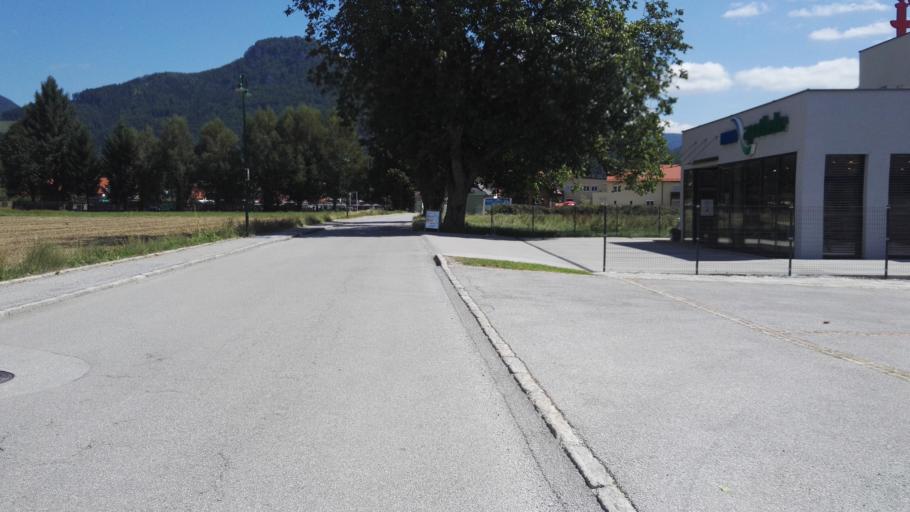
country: AT
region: Styria
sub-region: Politischer Bezirk Graz-Umgebung
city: Frohnleiten
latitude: 47.2659
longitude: 15.3163
